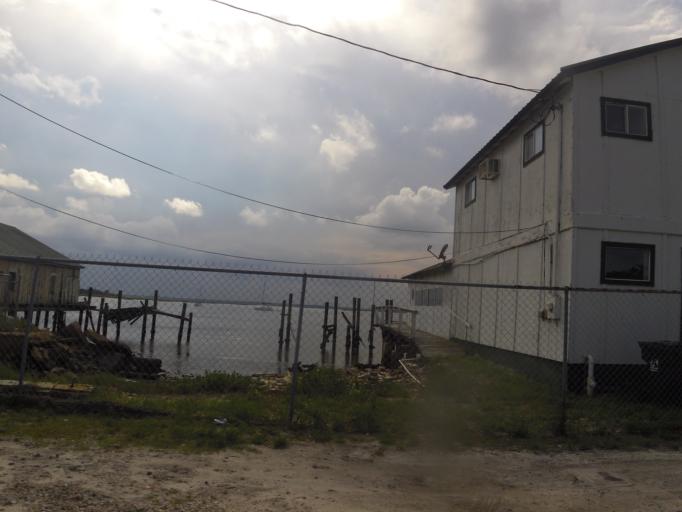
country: US
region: Florida
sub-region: Nassau County
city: Fernandina Beach
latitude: 30.6731
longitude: -81.4645
